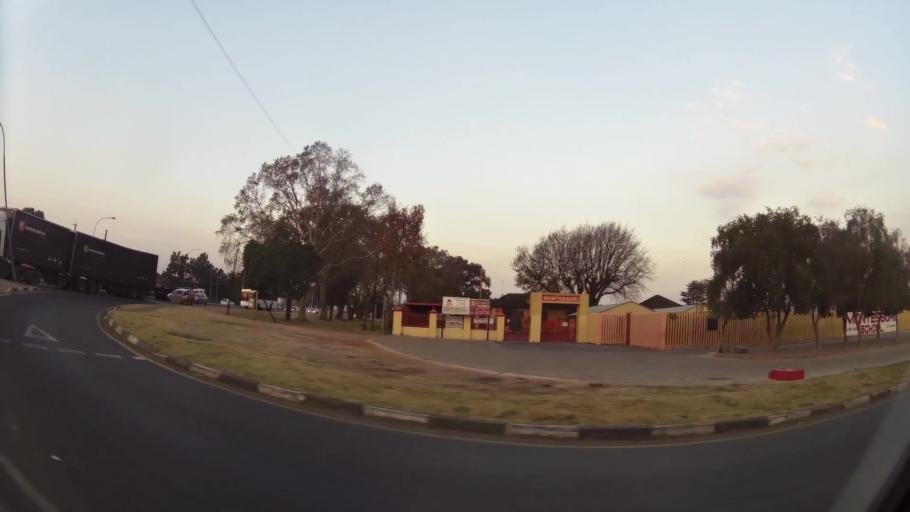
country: ZA
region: Gauteng
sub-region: Ekurhuleni Metropolitan Municipality
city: Springs
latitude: -26.2657
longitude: 28.4275
